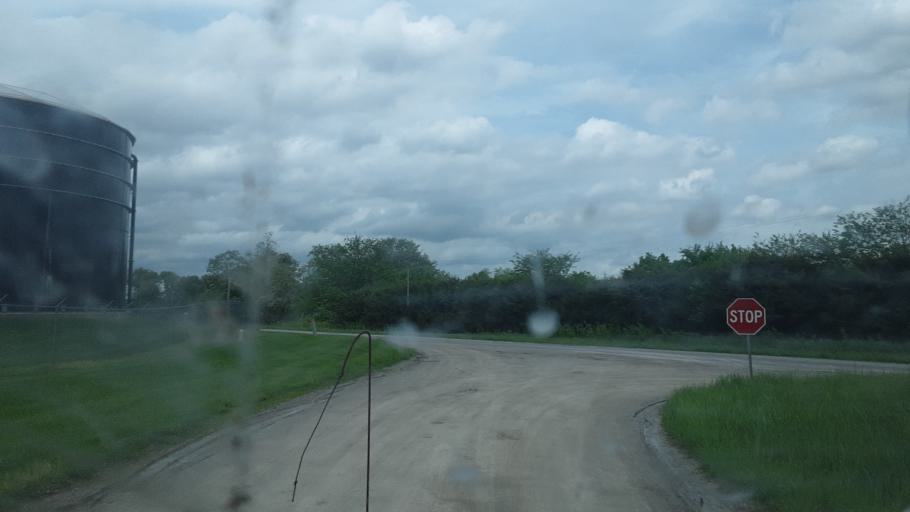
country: US
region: Missouri
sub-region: Clark County
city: Kahoka
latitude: 40.4437
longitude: -91.6099
